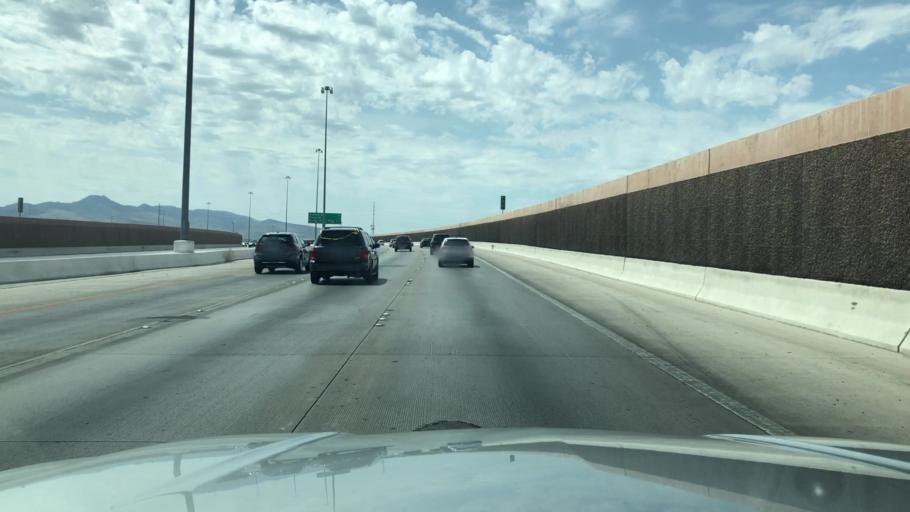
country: US
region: Nevada
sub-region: Clark County
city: Whitney
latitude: 36.0315
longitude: -115.1321
